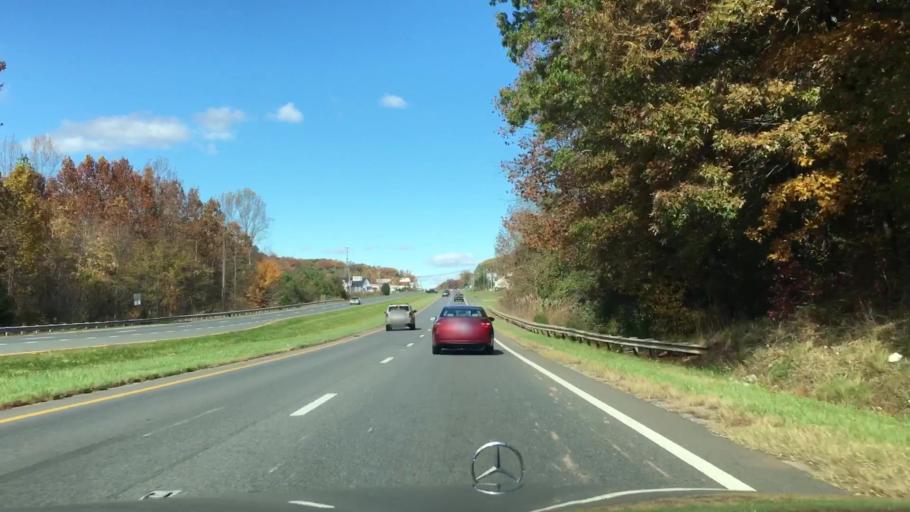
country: US
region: Virginia
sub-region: Campbell County
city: Rustburg
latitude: 37.2898
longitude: -79.1684
